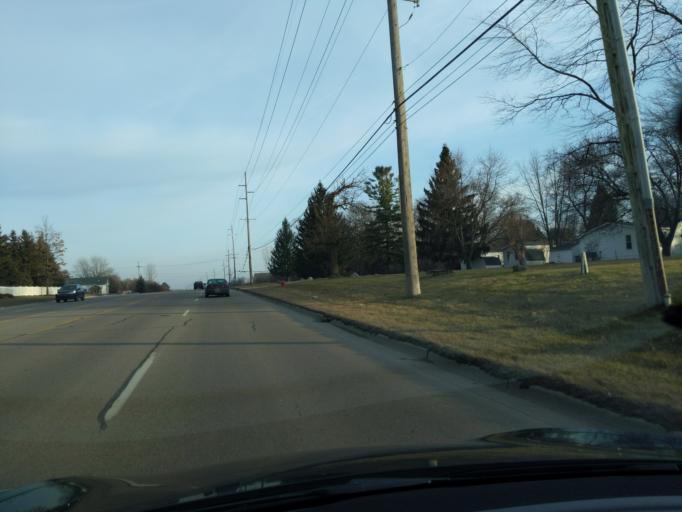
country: US
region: Michigan
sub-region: Livingston County
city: Brighton
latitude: 42.5707
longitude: -83.8213
